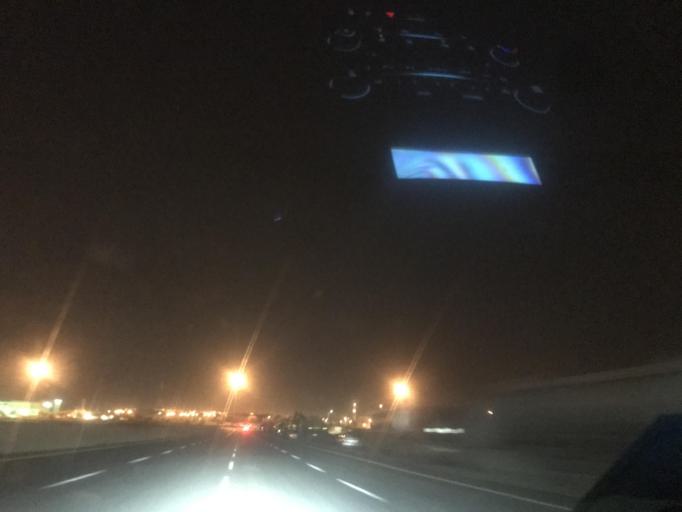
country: SA
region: Ar Riyad
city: Riyadh
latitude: 24.7609
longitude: 46.5835
